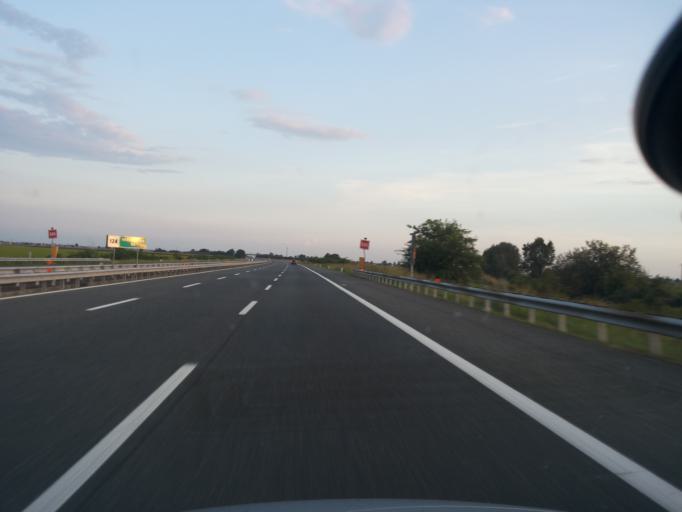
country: IT
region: Piedmont
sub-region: Provincia di Novara
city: Casalbeltrame
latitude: 45.4257
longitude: 8.4644
